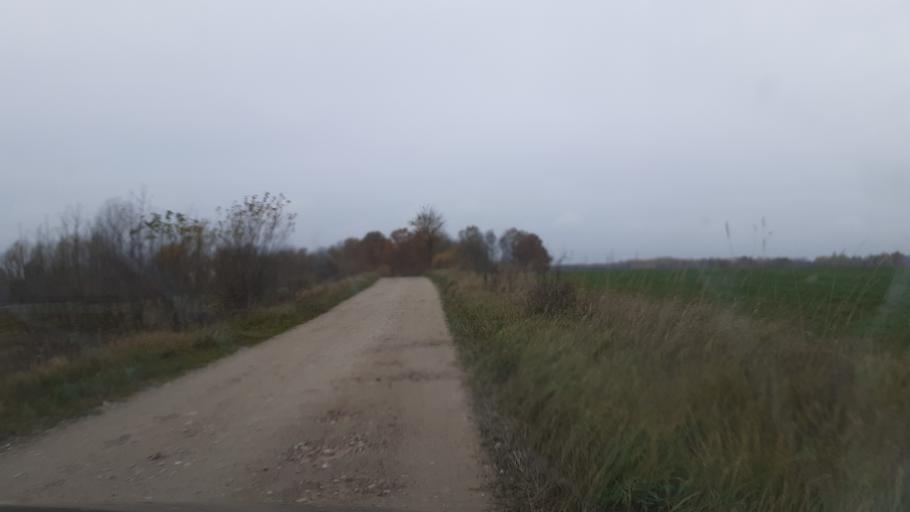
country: LV
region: Saldus Rajons
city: Saldus
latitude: 56.8680
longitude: 22.3417
